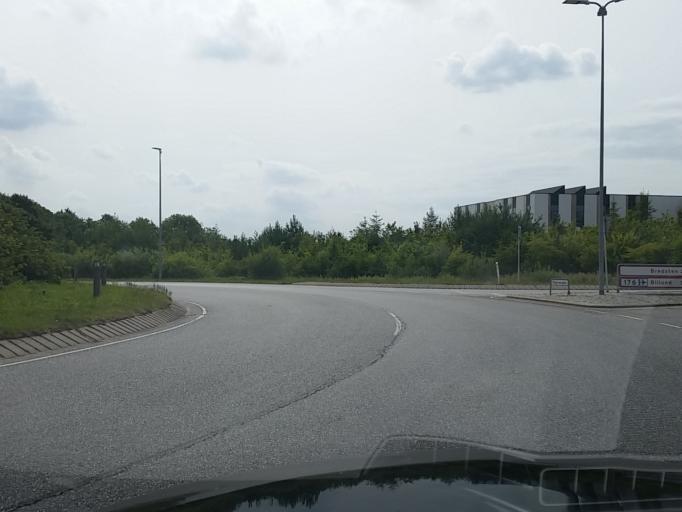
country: DK
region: South Denmark
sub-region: Kolding Kommune
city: Kolding
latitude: 55.5447
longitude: 9.4769
